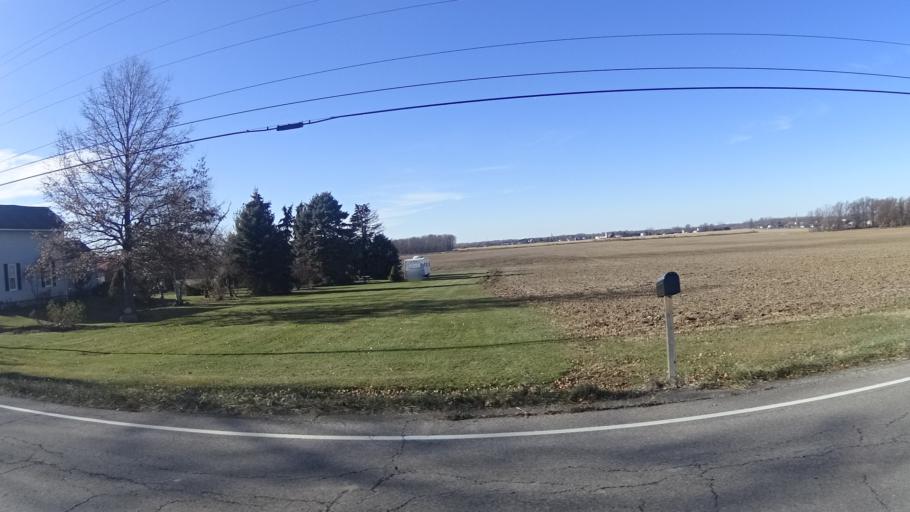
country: US
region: Ohio
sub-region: Lorain County
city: South Amherst
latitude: 41.3347
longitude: -82.3000
